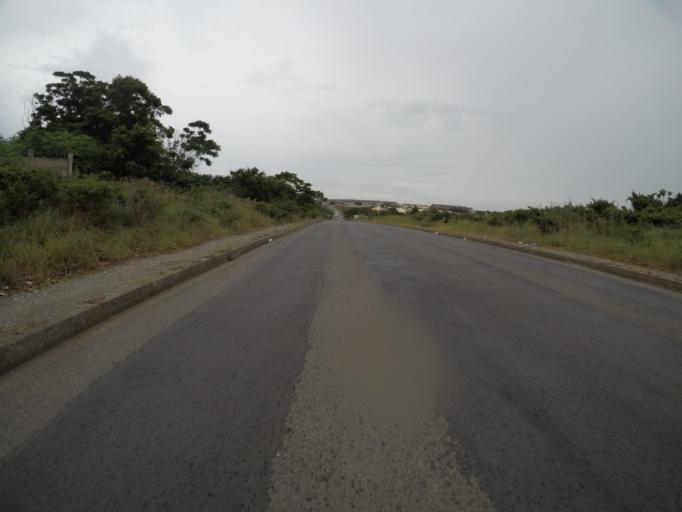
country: ZA
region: Eastern Cape
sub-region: Buffalo City Metropolitan Municipality
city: East London
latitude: -32.9682
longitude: 27.8281
